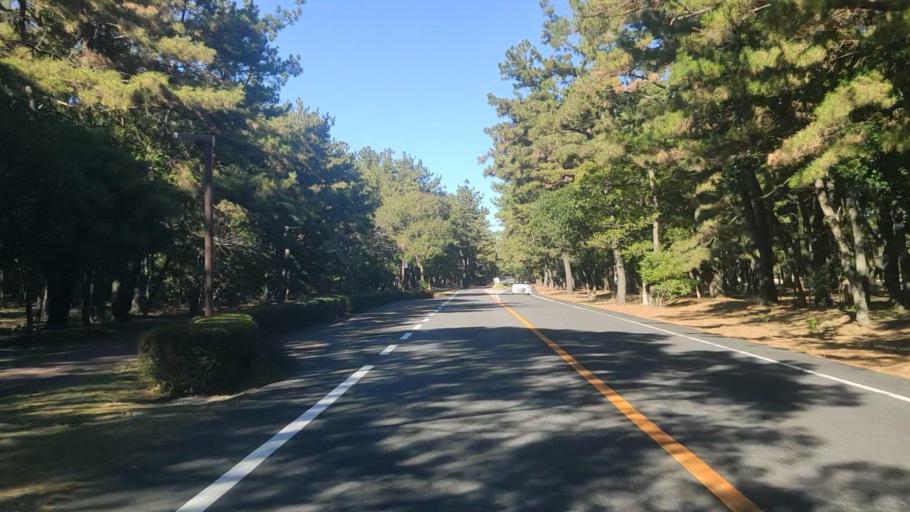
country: JP
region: Miyazaki
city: Miyazaki-shi
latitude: 31.9401
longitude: 131.4650
